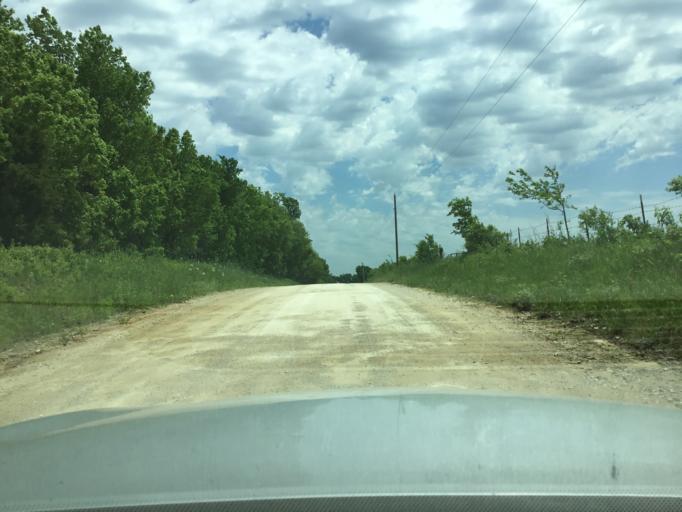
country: US
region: Kansas
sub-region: Montgomery County
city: Caney
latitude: 37.0952
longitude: -95.8133
